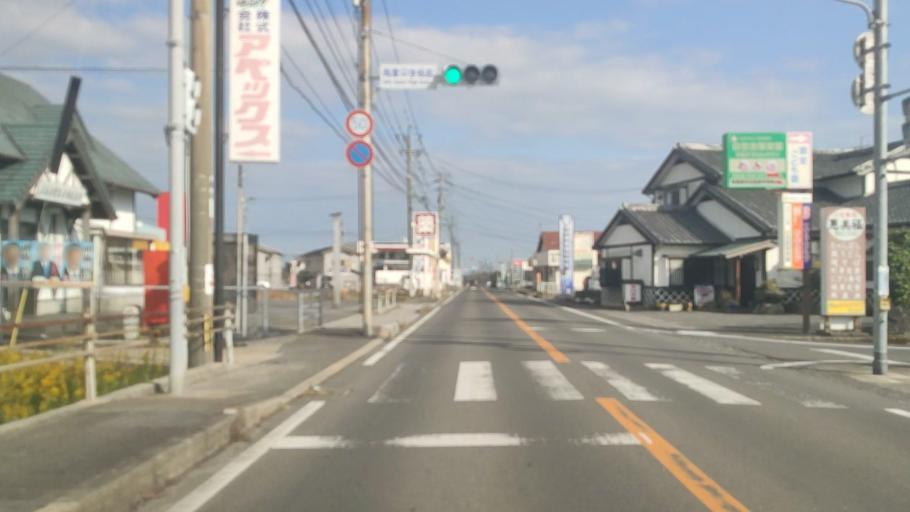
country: JP
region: Nagasaki
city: Shimabara
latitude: 32.6632
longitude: 130.3129
